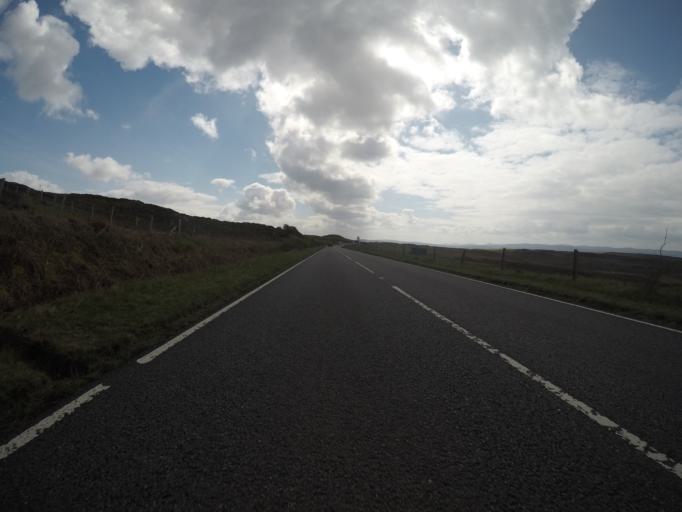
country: GB
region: Scotland
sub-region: Highland
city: Portree
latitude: 57.5581
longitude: -6.3636
